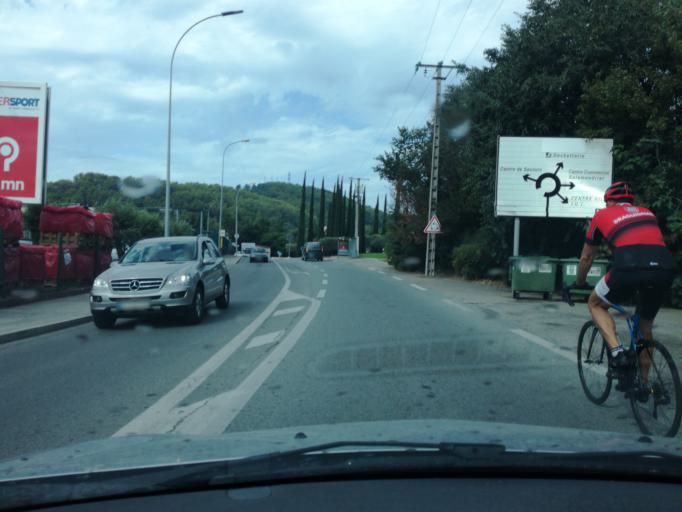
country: FR
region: Provence-Alpes-Cote d'Azur
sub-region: Departement du Var
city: Draguignan
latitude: 43.5268
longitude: 6.4567
